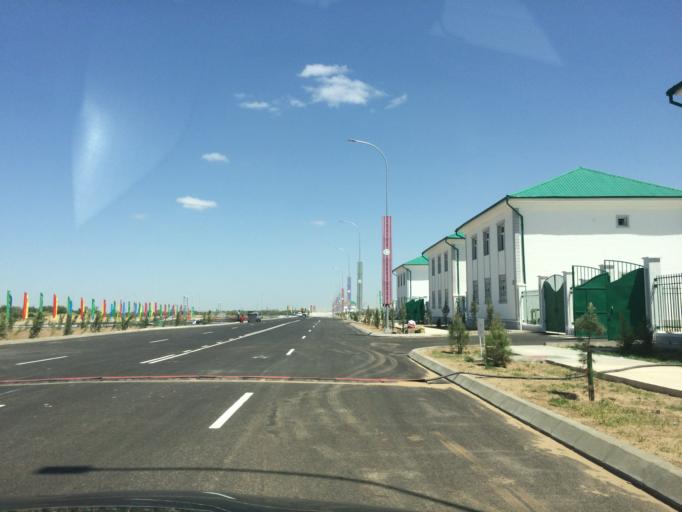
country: TM
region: Ahal
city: Abadan
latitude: 38.1001
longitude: 58.2887
